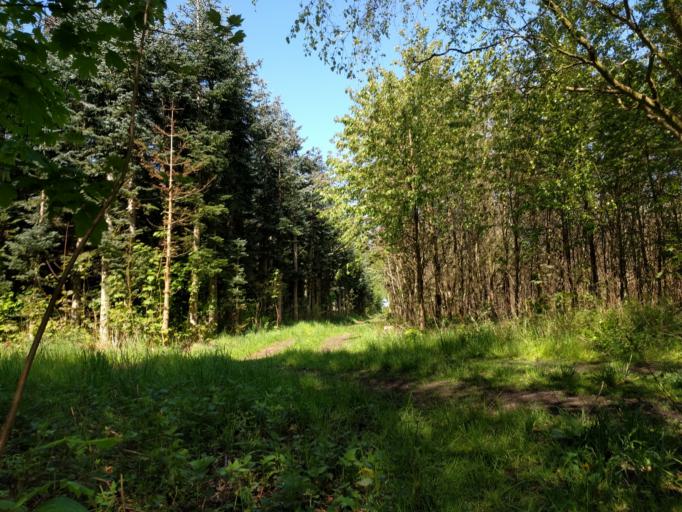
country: DK
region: South Denmark
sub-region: Kerteminde Kommune
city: Langeskov
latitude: 55.3937
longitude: 10.5530
